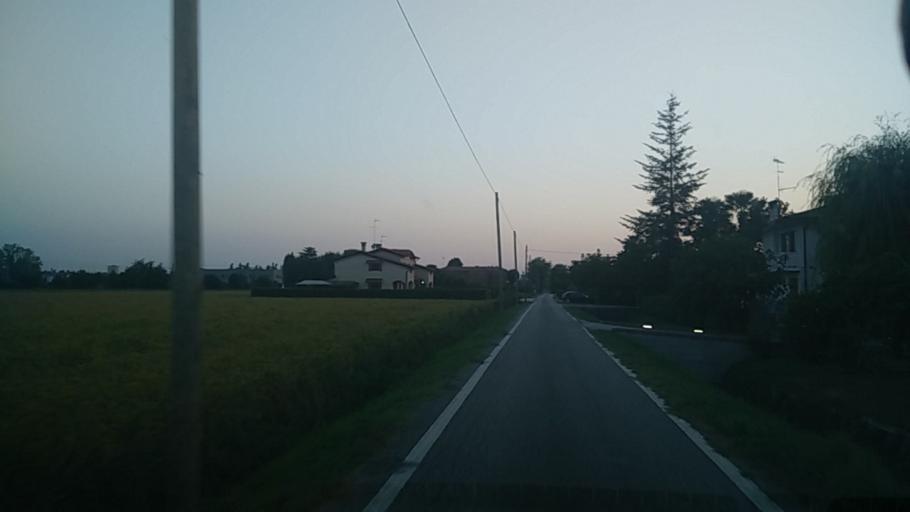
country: IT
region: Veneto
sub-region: Provincia di Venezia
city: San Dona di Piave
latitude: 45.6491
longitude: 12.5719
